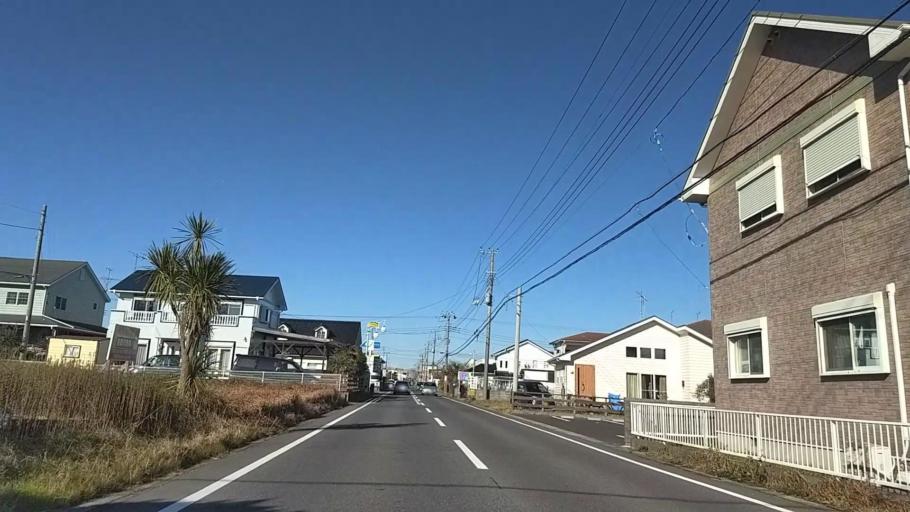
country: JP
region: Chiba
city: Ohara
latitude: 35.3555
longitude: 140.3889
